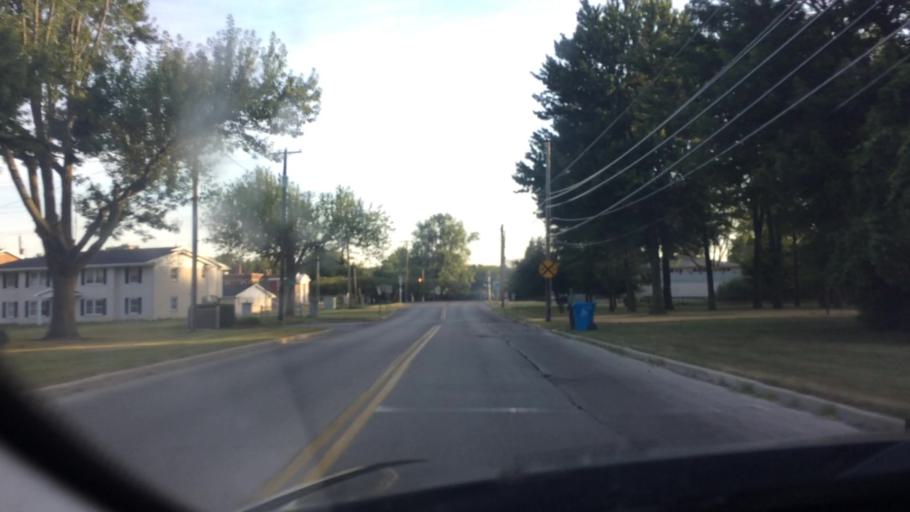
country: US
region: Ohio
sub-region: Lucas County
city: Ottawa Hills
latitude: 41.6597
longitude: -83.6411
